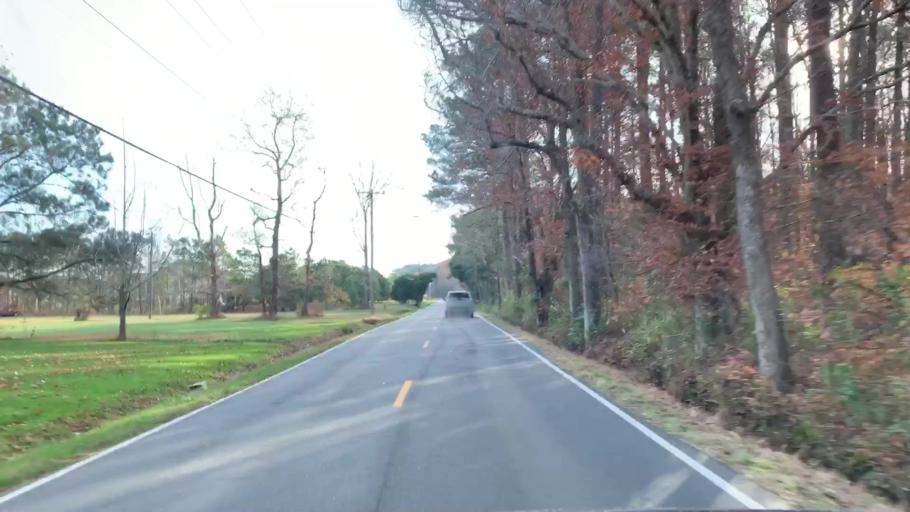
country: US
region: Virginia
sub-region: City of Virginia Beach
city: Virginia Beach
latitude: 36.7247
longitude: -76.0696
